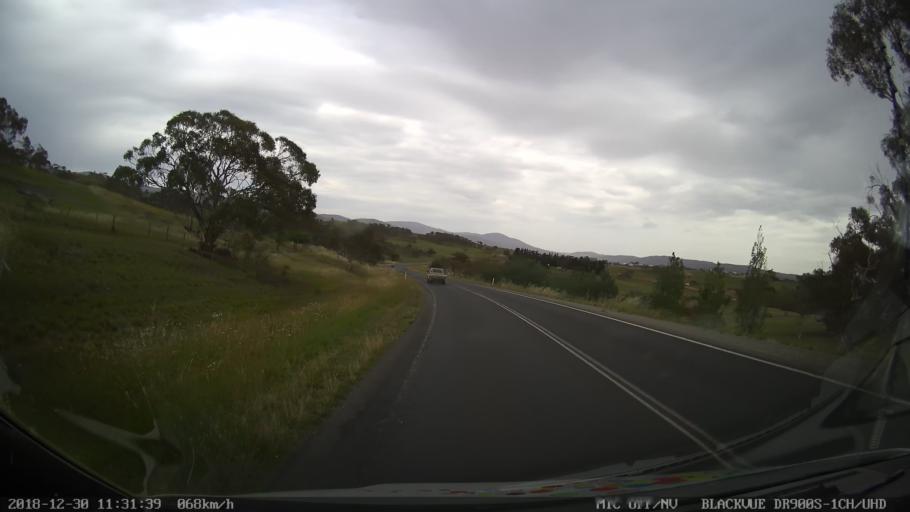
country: AU
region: New South Wales
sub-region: Snowy River
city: Jindabyne
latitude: -36.4295
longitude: 148.6100
